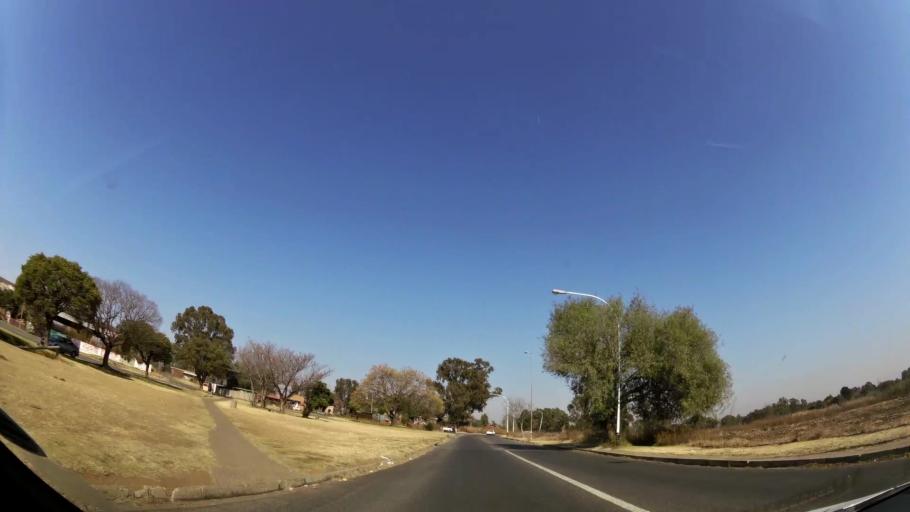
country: ZA
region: Gauteng
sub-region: Ekurhuleni Metropolitan Municipality
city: Boksburg
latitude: -26.2167
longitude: 28.2596
